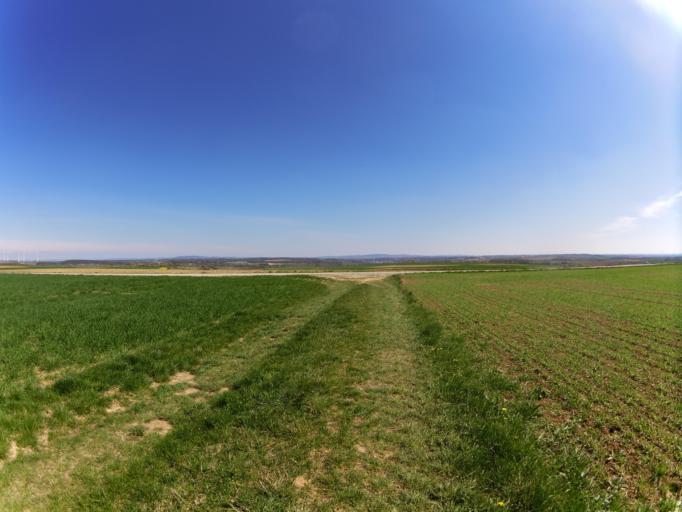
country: DE
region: Bavaria
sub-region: Regierungsbezirk Unterfranken
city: Winterhausen
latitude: 49.6858
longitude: 9.9987
